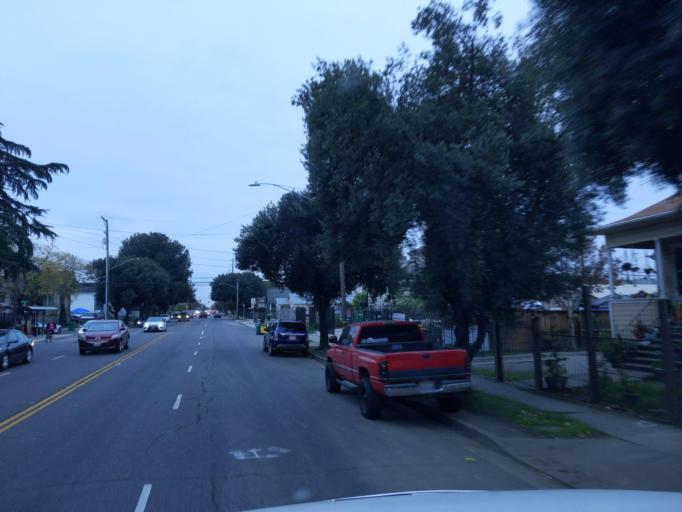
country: US
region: California
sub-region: San Joaquin County
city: Stockton
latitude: 37.9520
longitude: -121.2733
